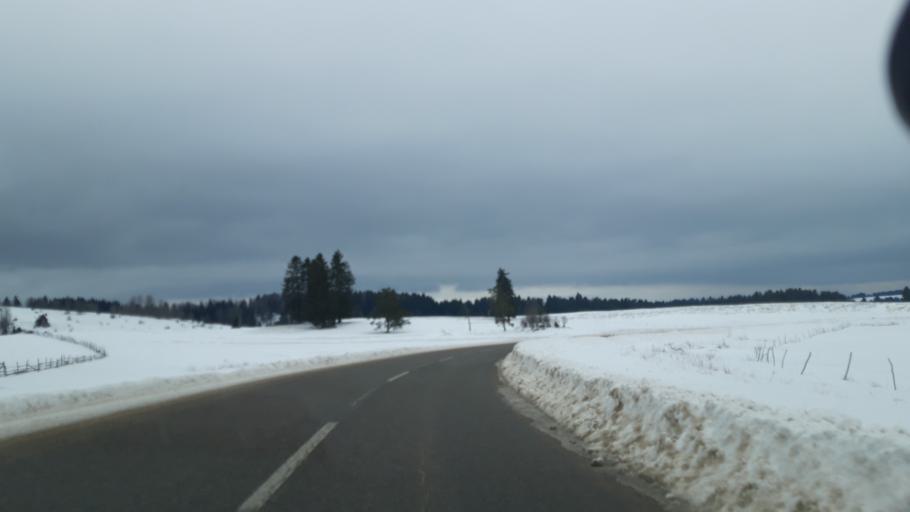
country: BA
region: Republika Srpska
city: Han Pijesak
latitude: 44.0312
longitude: 18.9238
